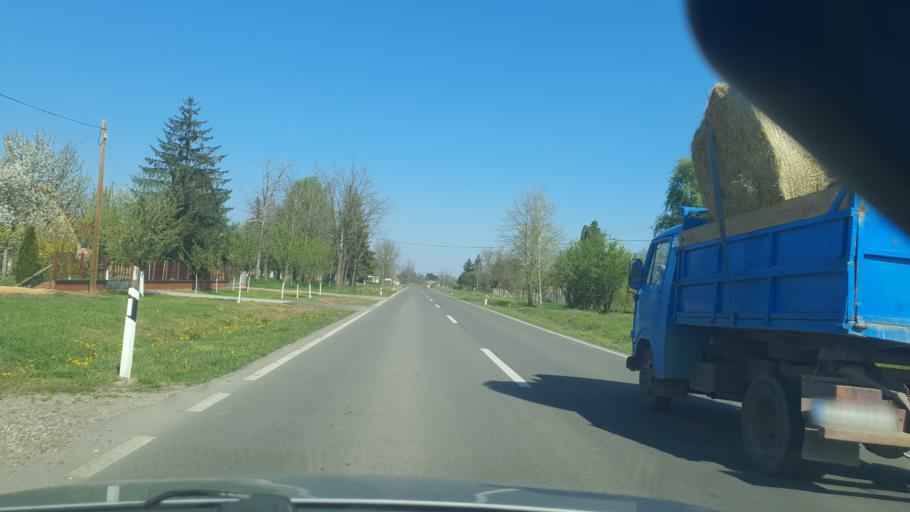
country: RS
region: Autonomna Pokrajina Vojvodina
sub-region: Zapadnobacki Okrug
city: Sombor
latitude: 45.8045
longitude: 19.0541
